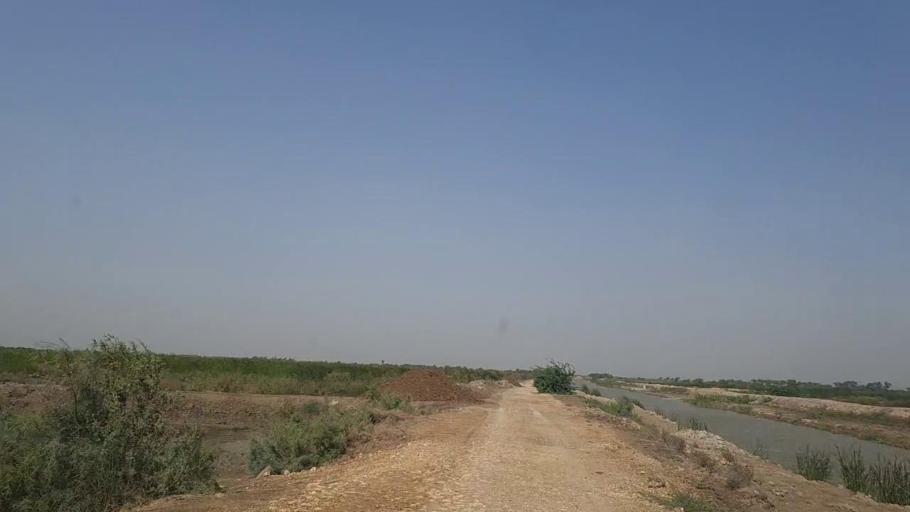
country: PK
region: Sindh
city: Daro Mehar
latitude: 24.7684
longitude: 68.1342
